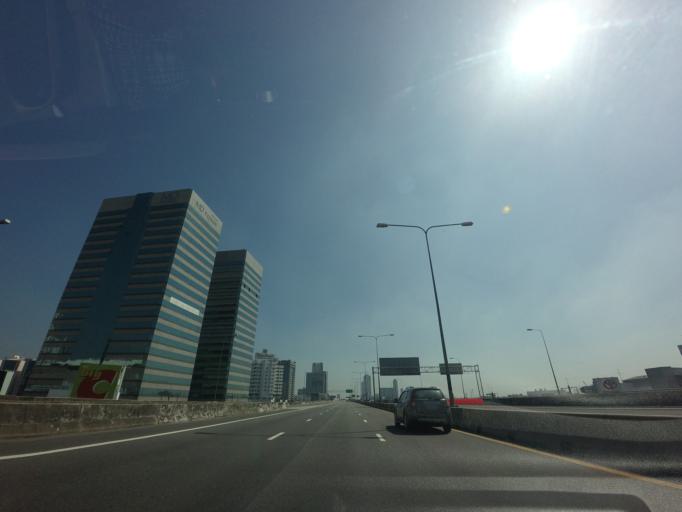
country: TH
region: Bangkok
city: Bang Na
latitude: 13.6677
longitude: 100.6352
